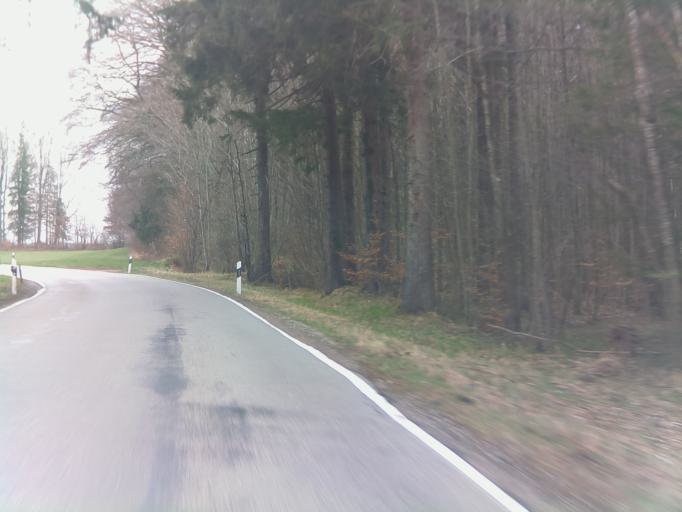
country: DE
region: Bavaria
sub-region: Upper Bavaria
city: Bobing
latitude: 47.7664
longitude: 11.0089
